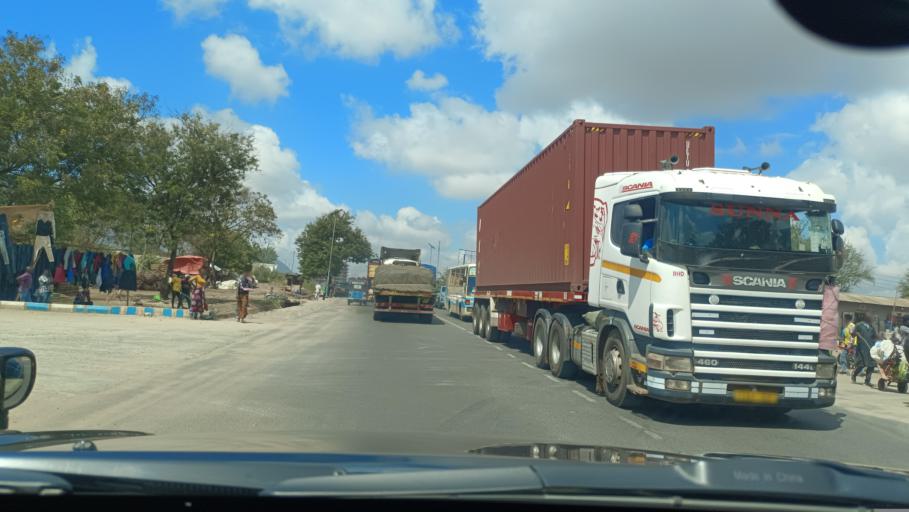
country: TZ
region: Morogoro
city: Morogoro
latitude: -6.8052
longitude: 37.6616
